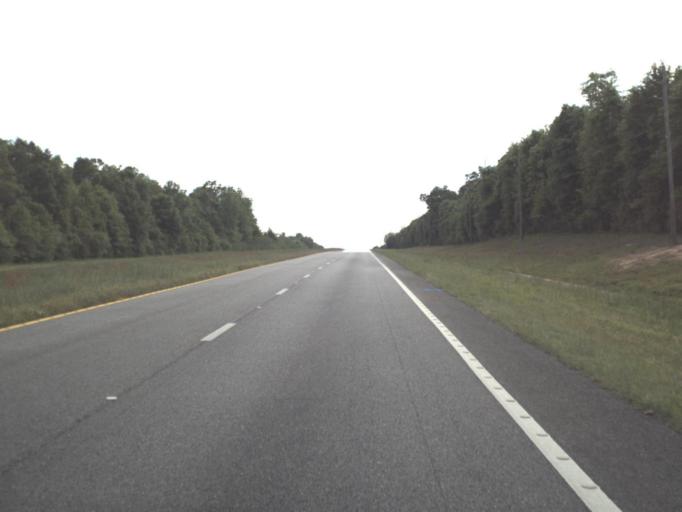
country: US
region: Florida
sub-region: Escambia County
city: Molino
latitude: 30.7587
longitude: -87.3432
